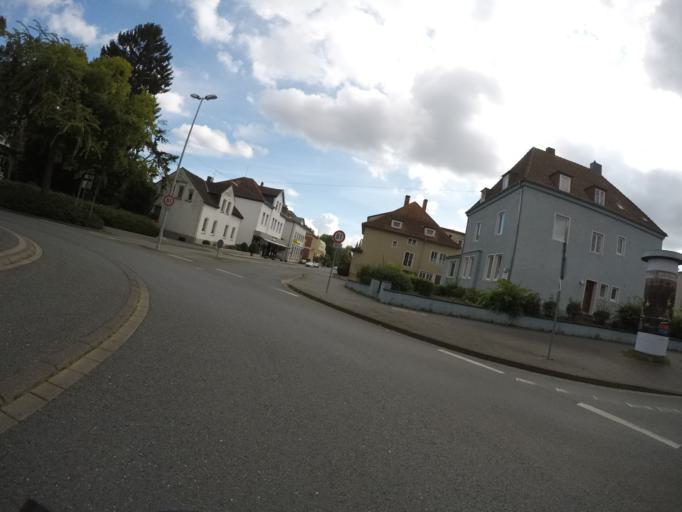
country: DE
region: North Rhine-Westphalia
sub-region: Regierungsbezirk Detmold
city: Herford
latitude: 52.1201
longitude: 8.6670
